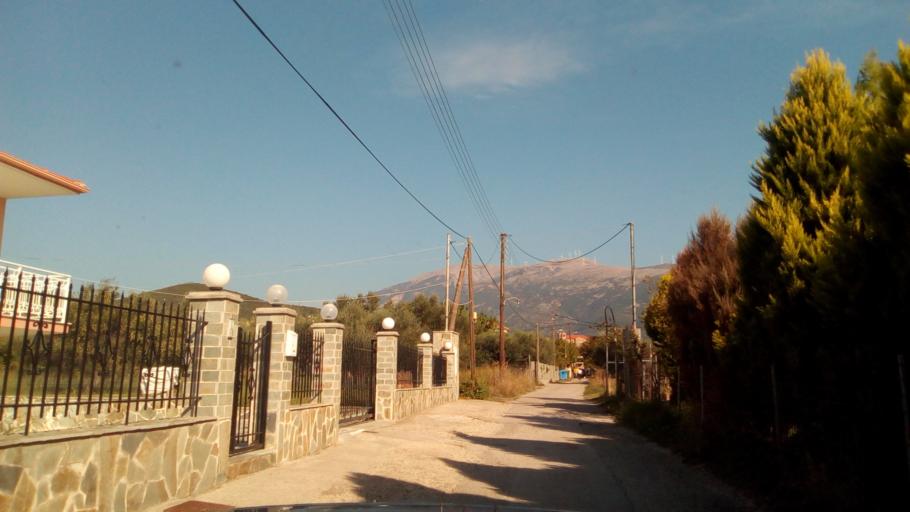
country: GR
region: West Greece
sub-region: Nomos Aitolias kai Akarnanias
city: Nafpaktos
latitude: 38.3758
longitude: 21.7982
